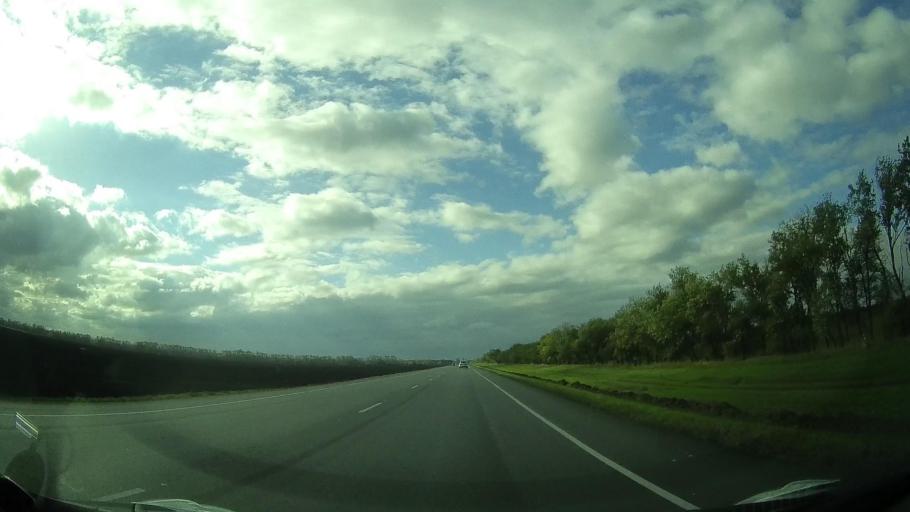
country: RU
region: Rostov
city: Tselina
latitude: 46.5322
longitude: 40.9345
